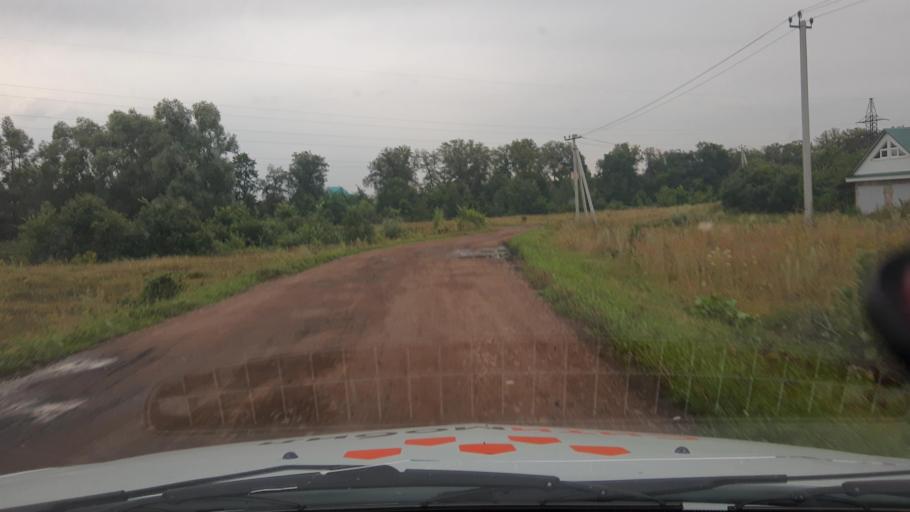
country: RU
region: Bashkortostan
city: Ufa
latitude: 54.5700
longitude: 55.9490
